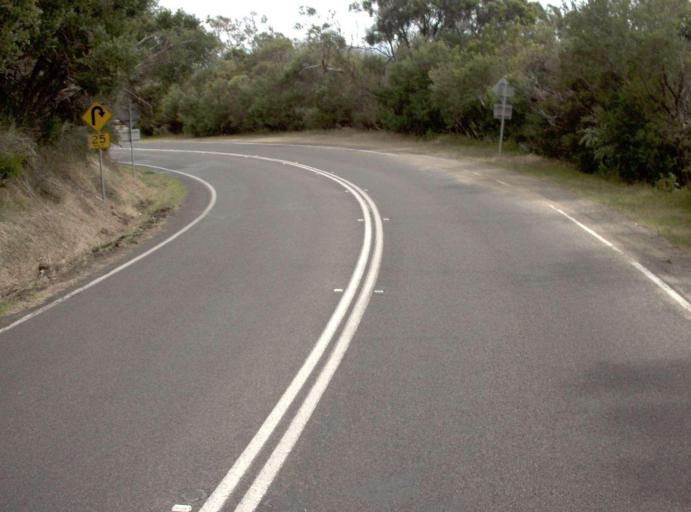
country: AU
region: Victoria
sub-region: Mornington Peninsula
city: Dromana
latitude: -38.3462
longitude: 144.9516
